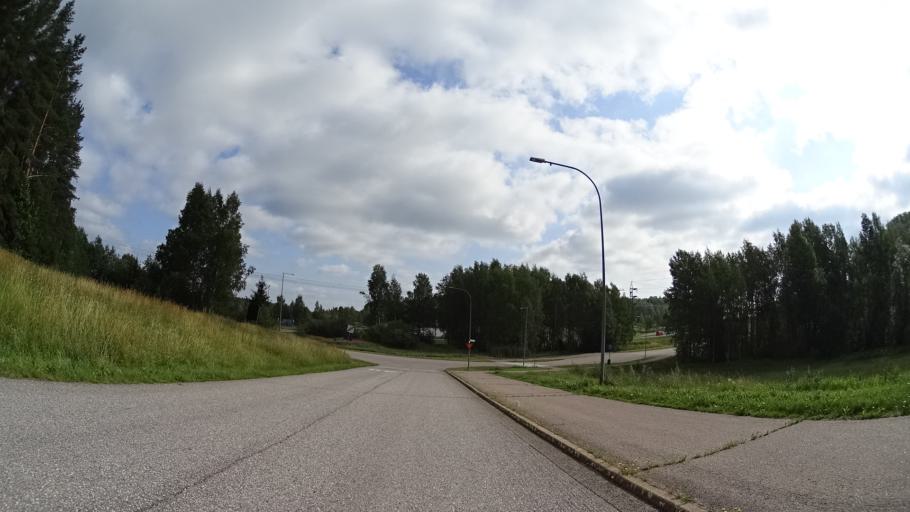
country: FI
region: Uusimaa
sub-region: Helsinki
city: Kilo
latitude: 60.2726
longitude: 24.7894
